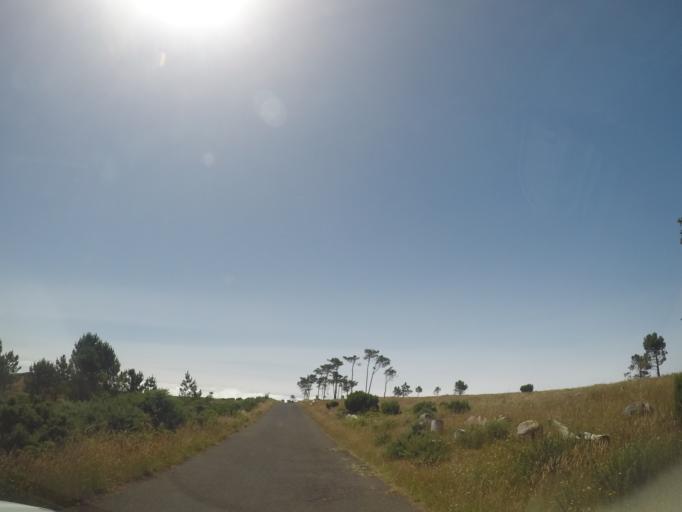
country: PT
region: Madeira
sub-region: Funchal
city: Nossa Senhora do Monte
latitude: 32.7177
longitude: -16.9131
